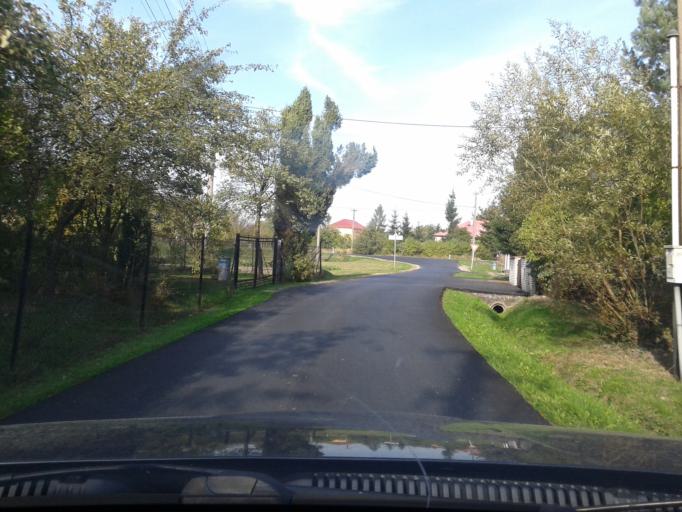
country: CZ
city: Detmarovice
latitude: 49.8835
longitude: 18.4762
